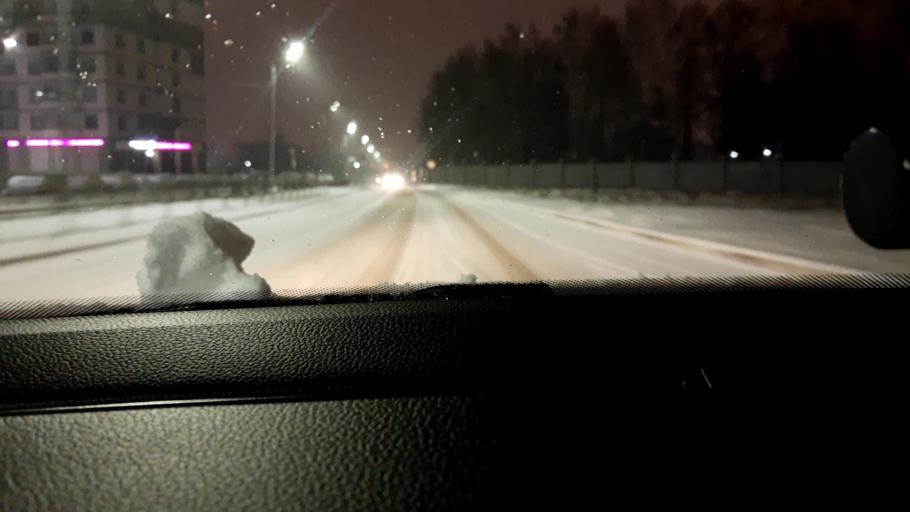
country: RU
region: Moskovskaya
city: Mytishchi
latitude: 55.9283
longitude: 37.7364
